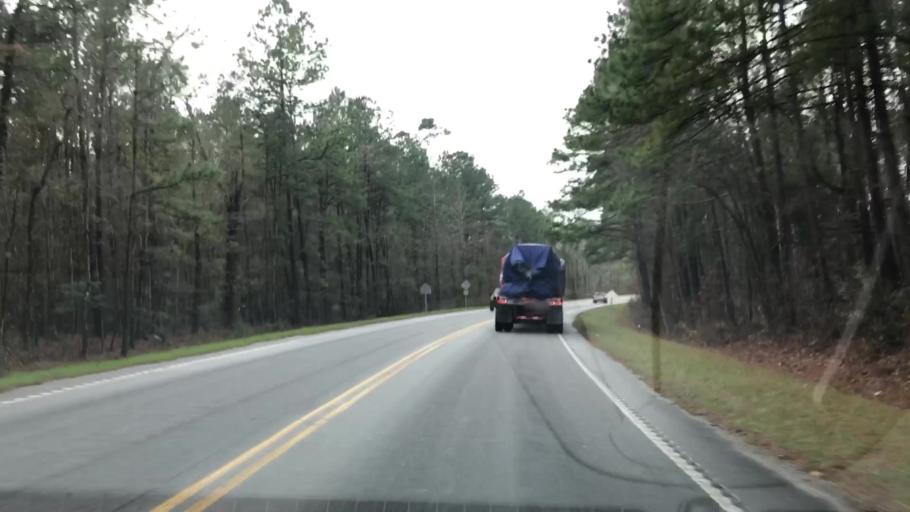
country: US
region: South Carolina
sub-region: Berkeley County
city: Bonneau Beach
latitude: 33.2698
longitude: -79.9001
